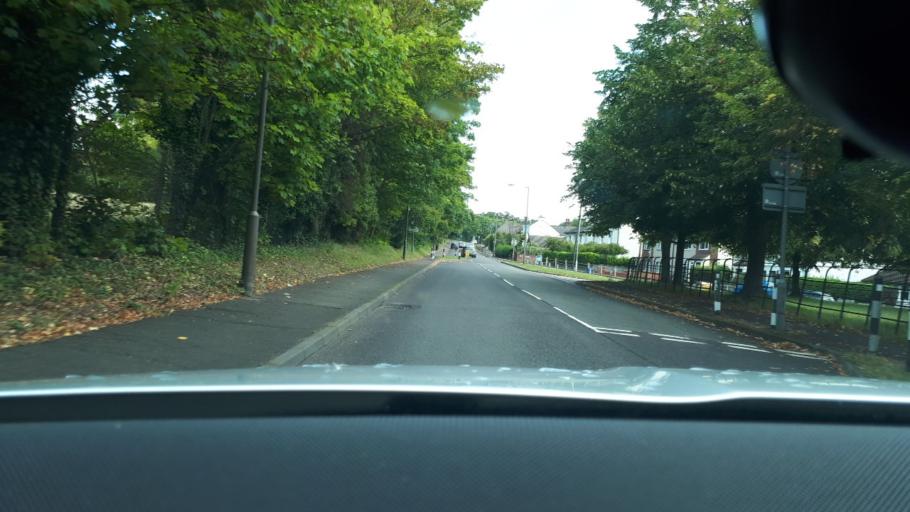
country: GB
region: England
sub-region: Kent
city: Swanley
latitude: 51.4125
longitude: 0.1828
